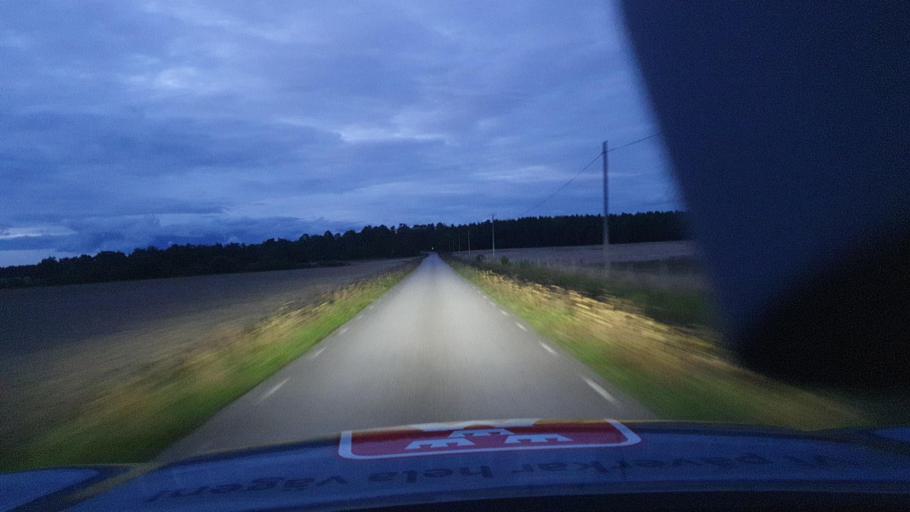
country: SE
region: Gotland
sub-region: Gotland
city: Slite
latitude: 57.7616
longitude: 18.6427
